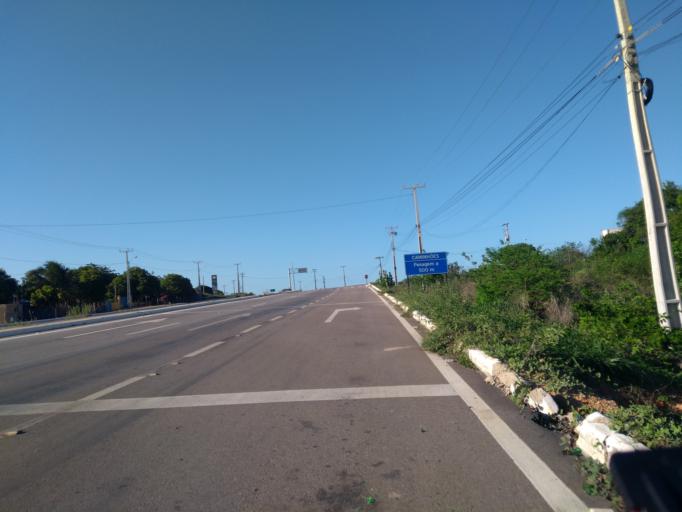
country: BR
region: Ceara
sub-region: Aracati
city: Aracati
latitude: -4.5685
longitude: -37.7918
